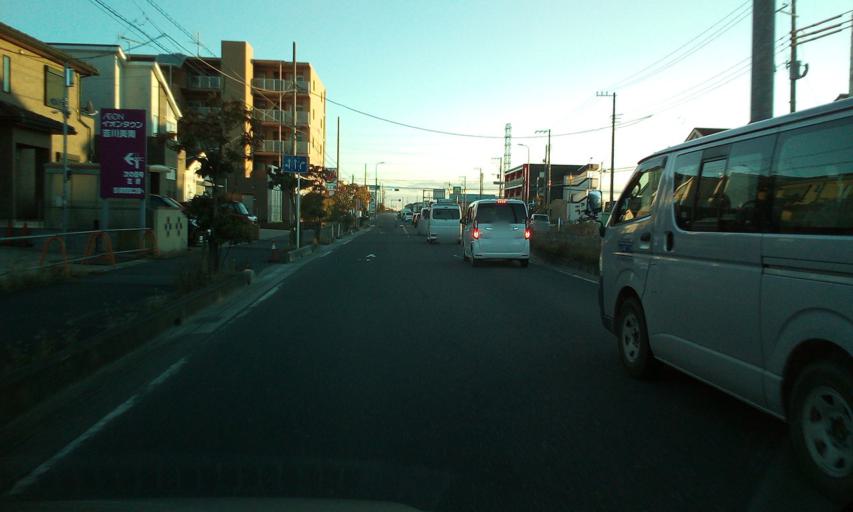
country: JP
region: Saitama
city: Yoshikawa
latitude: 35.8657
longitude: 139.8483
